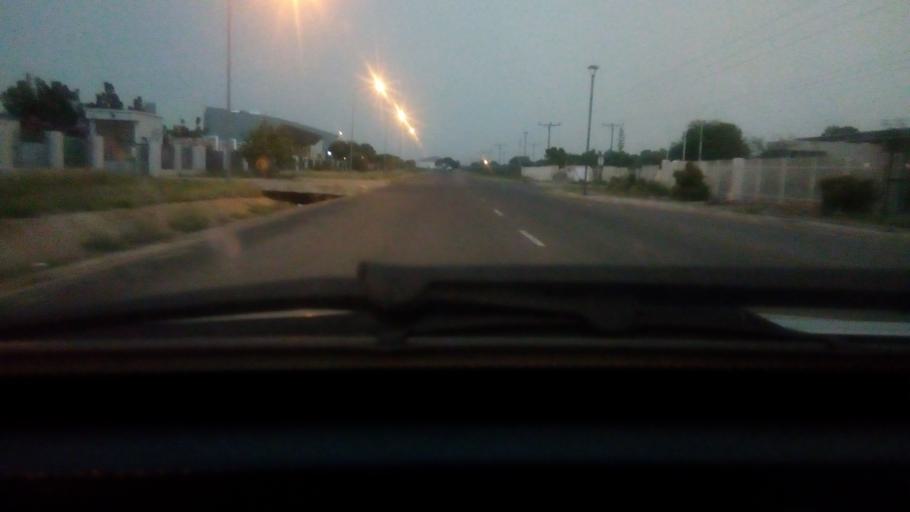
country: BW
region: Kweneng
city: Mmopone
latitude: -24.5890
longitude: 25.9108
